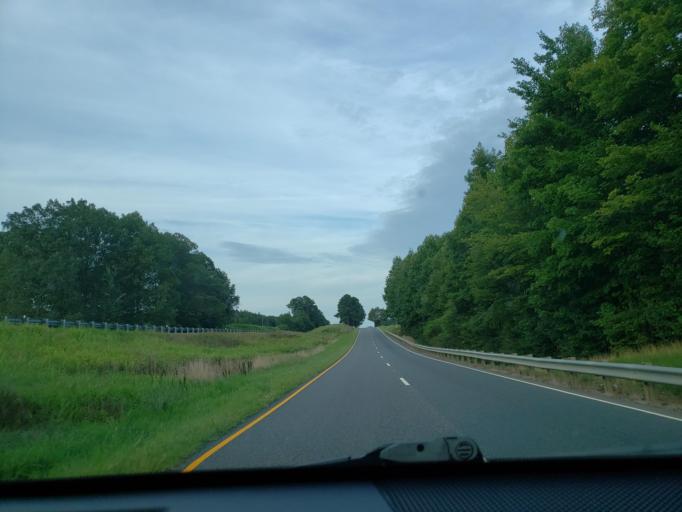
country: US
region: Virginia
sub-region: Brunswick County
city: Lawrenceville
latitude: 36.7227
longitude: -77.9468
